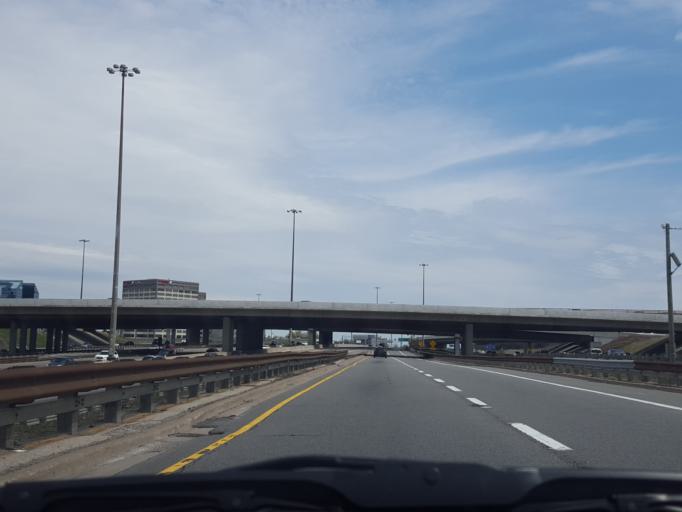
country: CA
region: Ontario
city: Willowdale
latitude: 43.7671
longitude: -79.3410
